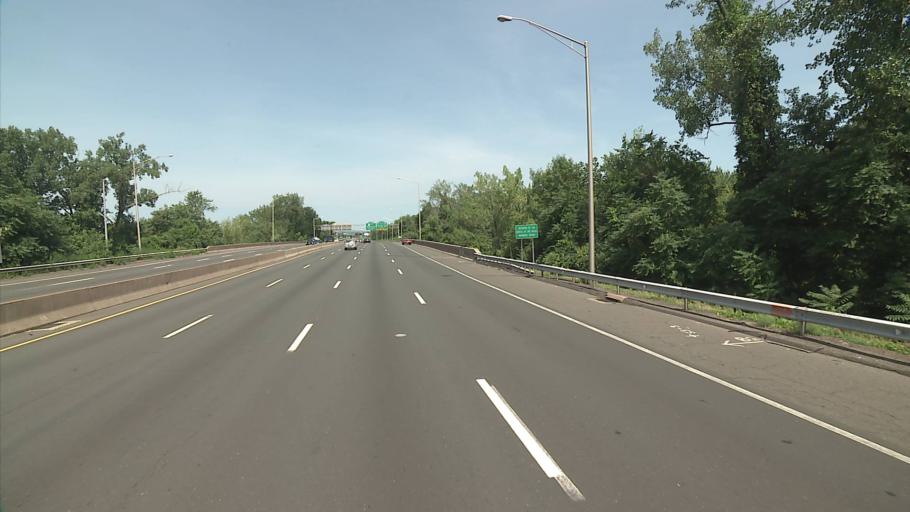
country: US
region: Connecticut
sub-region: Hartford County
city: Wethersfield
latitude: 41.7250
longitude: -72.6531
